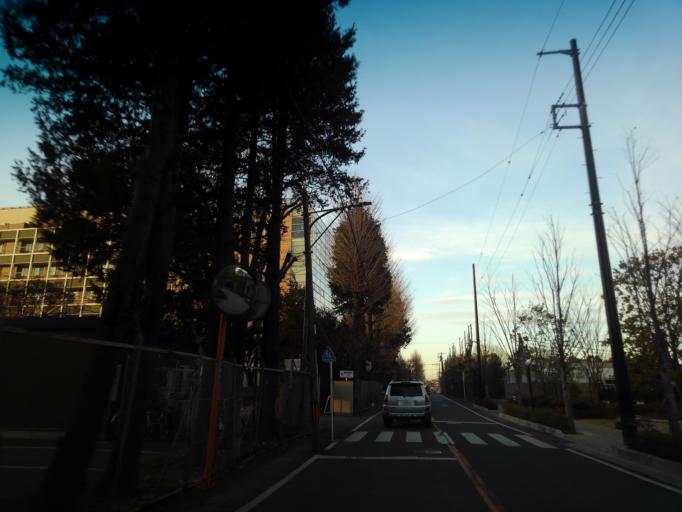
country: JP
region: Tokyo
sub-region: Machida-shi
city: Machida
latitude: 35.5752
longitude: 139.3923
